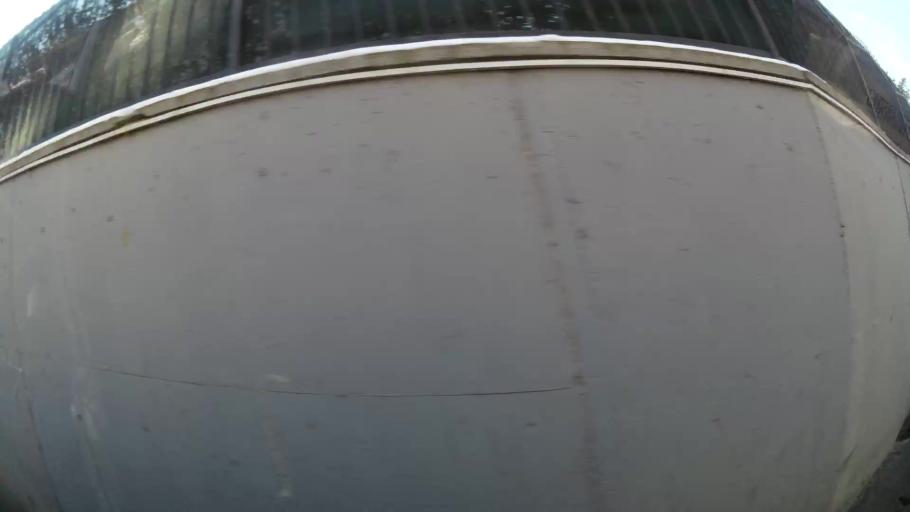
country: MK
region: Karpos
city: Skopje
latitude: 41.9832
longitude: 21.4205
